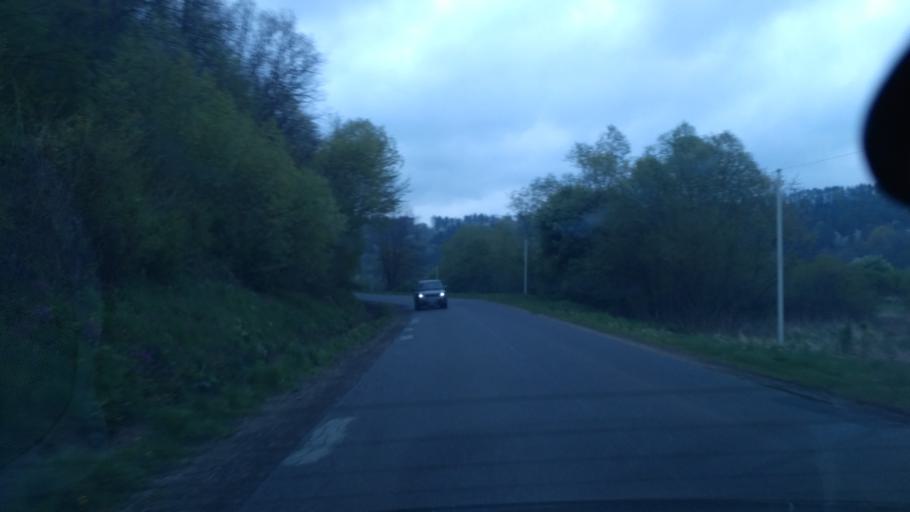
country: PL
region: Subcarpathian Voivodeship
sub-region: Powiat brzozowski
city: Nozdrzec
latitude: 49.7219
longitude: 22.2185
